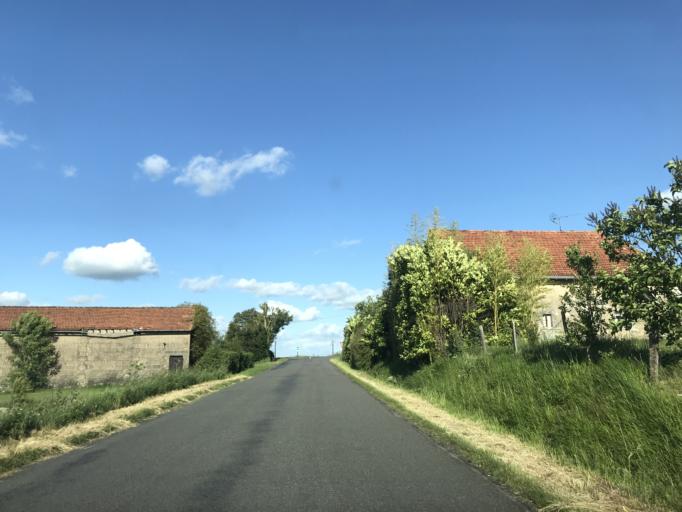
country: FR
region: Poitou-Charentes
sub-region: Departement de la Charente
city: Chalais
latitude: 45.2694
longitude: 0.0189
